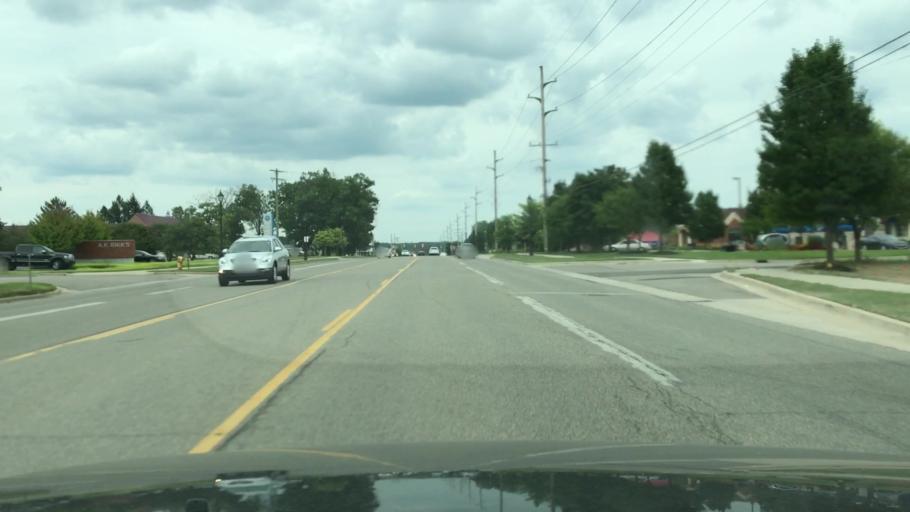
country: US
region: Michigan
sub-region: Kent County
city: Forest Hills
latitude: 42.9131
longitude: -85.5128
